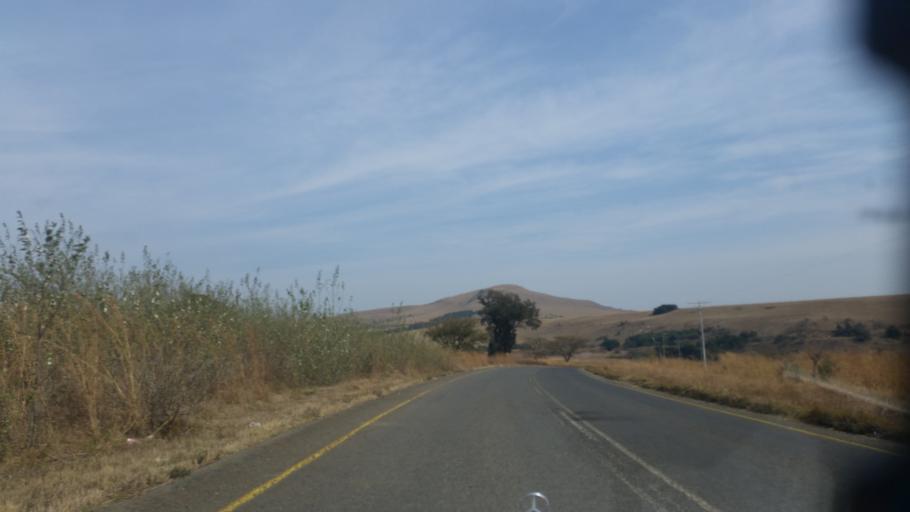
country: ZA
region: KwaZulu-Natal
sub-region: uThukela District Municipality
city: Estcourt
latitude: -29.0720
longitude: 29.9441
